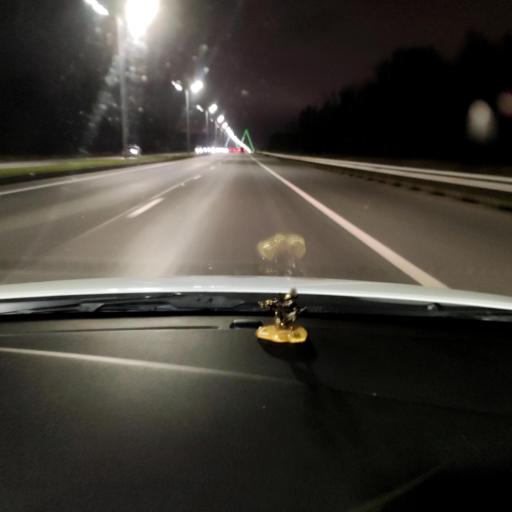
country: RU
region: Tatarstan
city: Stolbishchi
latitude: 55.7064
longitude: 49.2196
